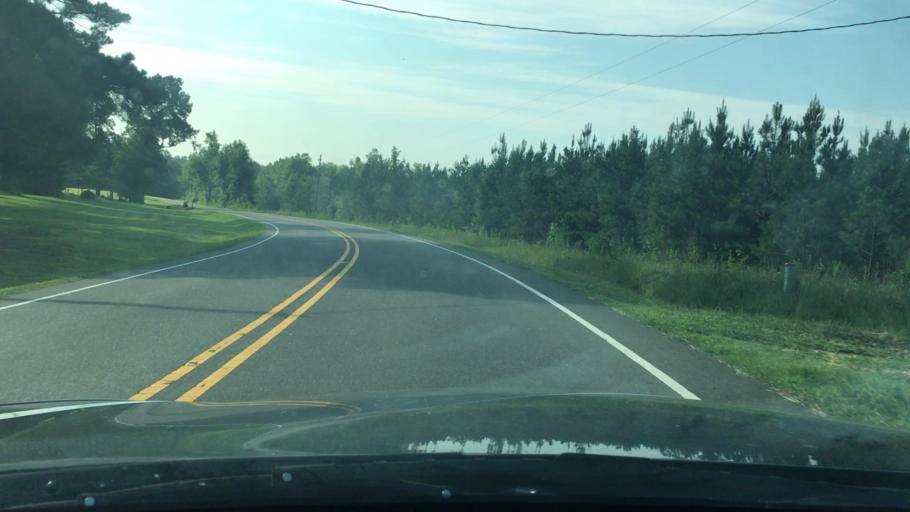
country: US
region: North Carolina
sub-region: Alamance County
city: Green Level
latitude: 36.2582
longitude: -79.3368
